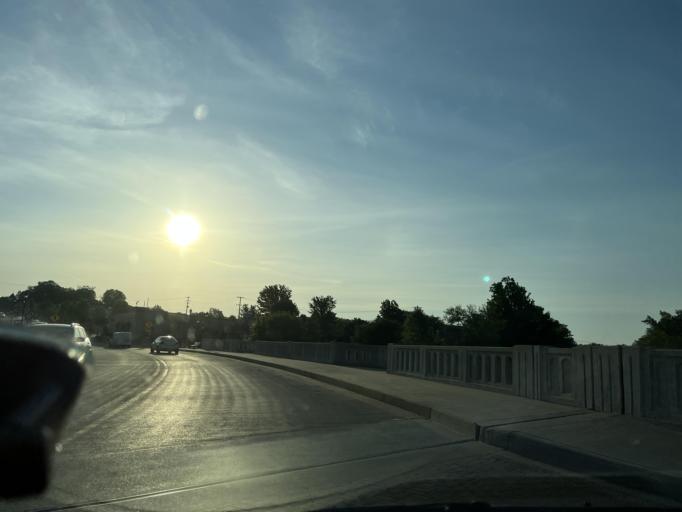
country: US
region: Michigan
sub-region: Barry County
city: Middleville
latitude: 42.7110
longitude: -85.4659
